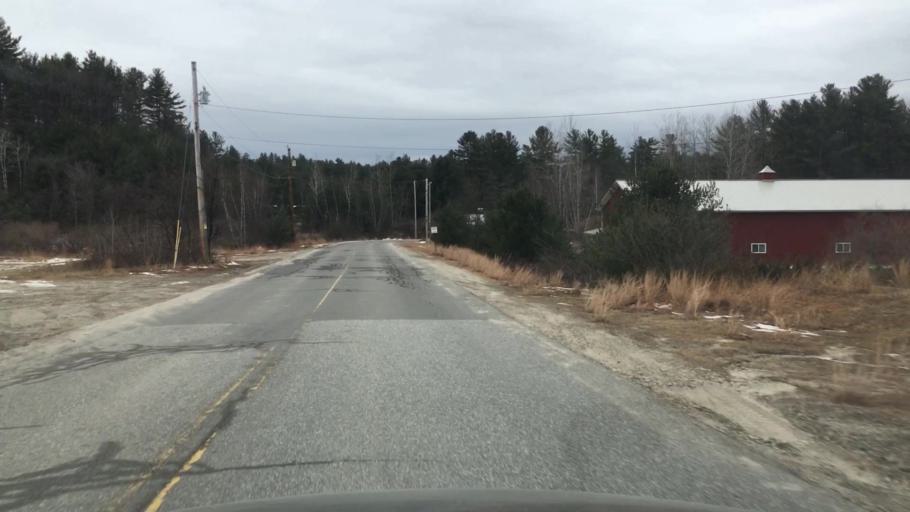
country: US
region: New Hampshire
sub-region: Hillsborough County
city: New Boston
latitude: 42.9986
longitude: -71.6613
